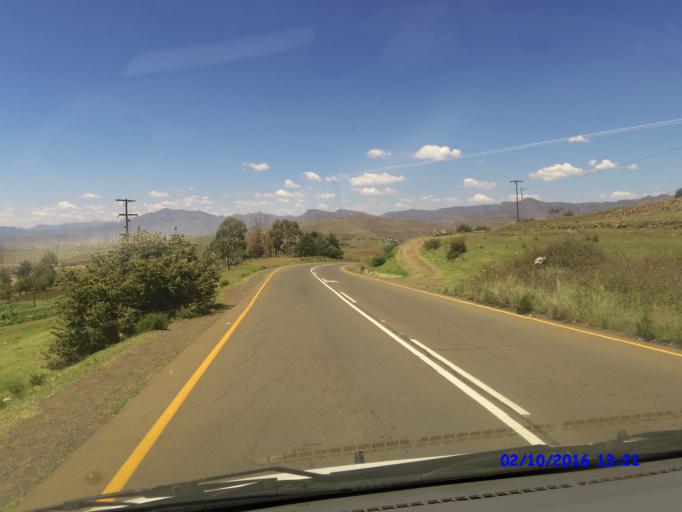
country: LS
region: Maseru
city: Nako
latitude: -29.4183
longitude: 27.7153
